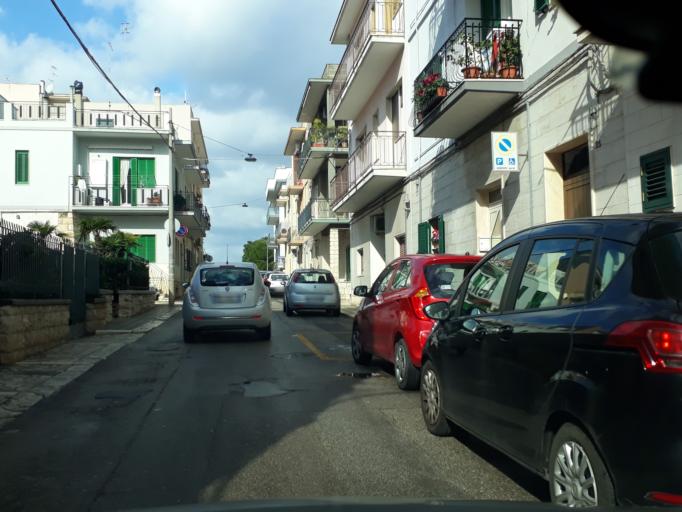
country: IT
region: Apulia
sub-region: Provincia di Brindisi
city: Fasano
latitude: 40.8320
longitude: 17.3544
